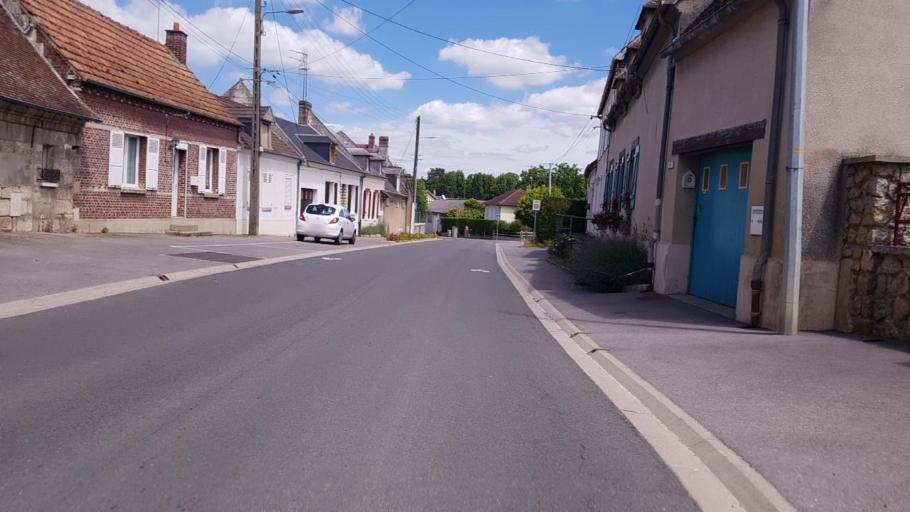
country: FR
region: Picardie
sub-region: Departement de l'Oise
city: Montmacq
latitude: 49.4796
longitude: 2.9522
